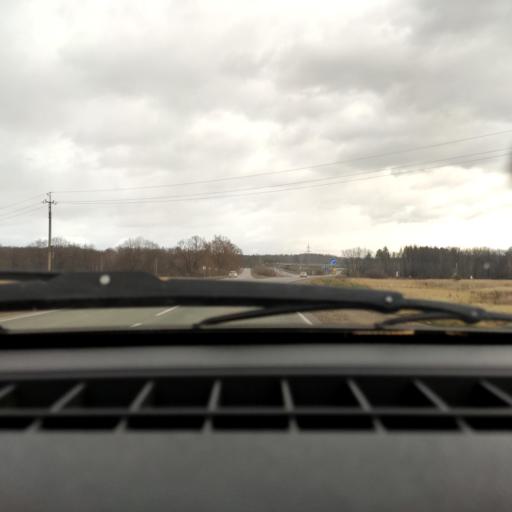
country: RU
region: Bashkortostan
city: Iglino
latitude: 54.7475
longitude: 56.2964
